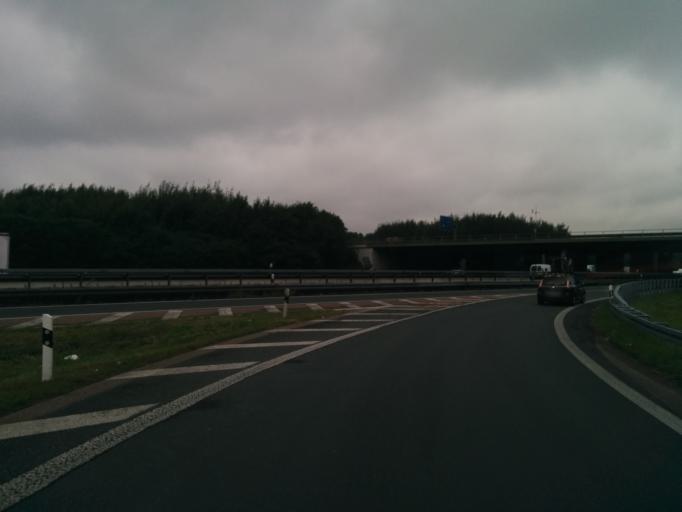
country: DE
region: North Rhine-Westphalia
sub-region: Regierungsbezirk Arnsberg
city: Holzwickede
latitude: 51.5212
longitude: 7.6584
